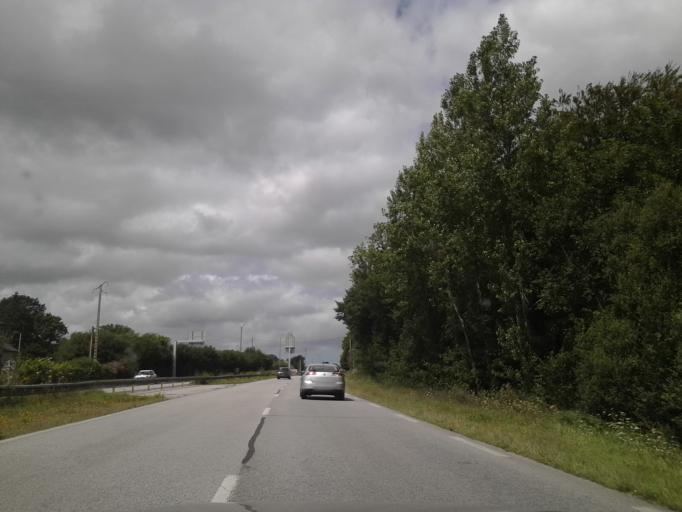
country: FR
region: Lower Normandy
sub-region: Departement de la Manche
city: Brix
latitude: 49.5691
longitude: -1.5738
